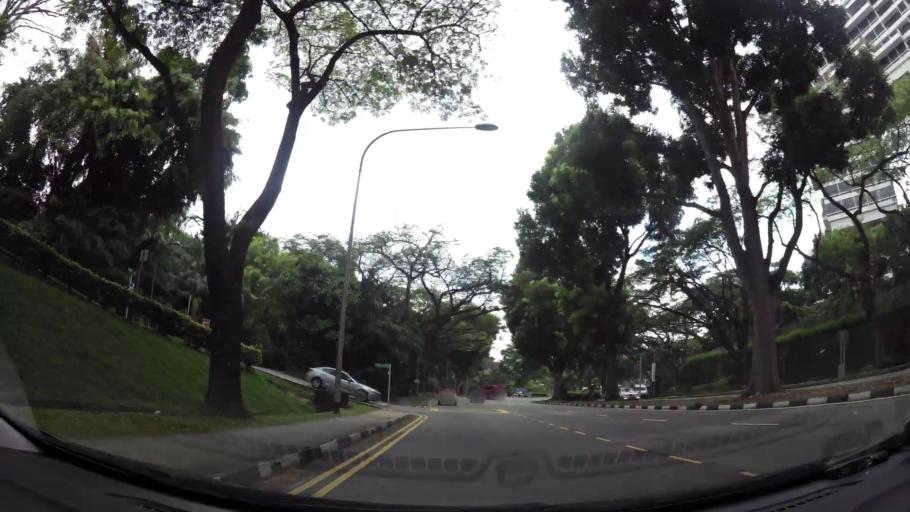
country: SG
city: Singapore
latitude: 1.2823
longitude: 103.8014
